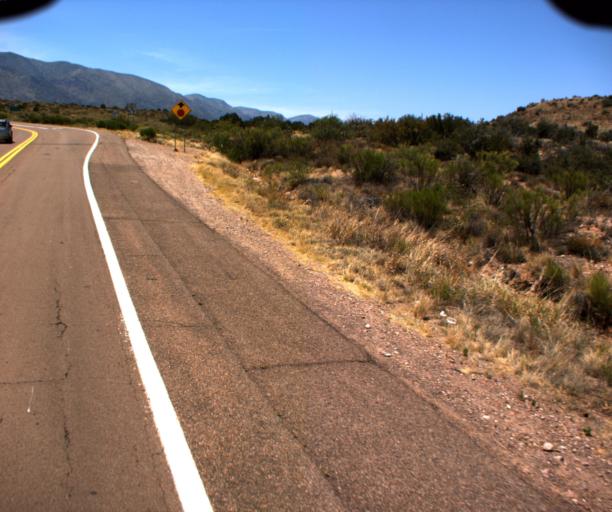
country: US
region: Arizona
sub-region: Gila County
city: Payson
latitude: 34.0362
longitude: -111.3655
